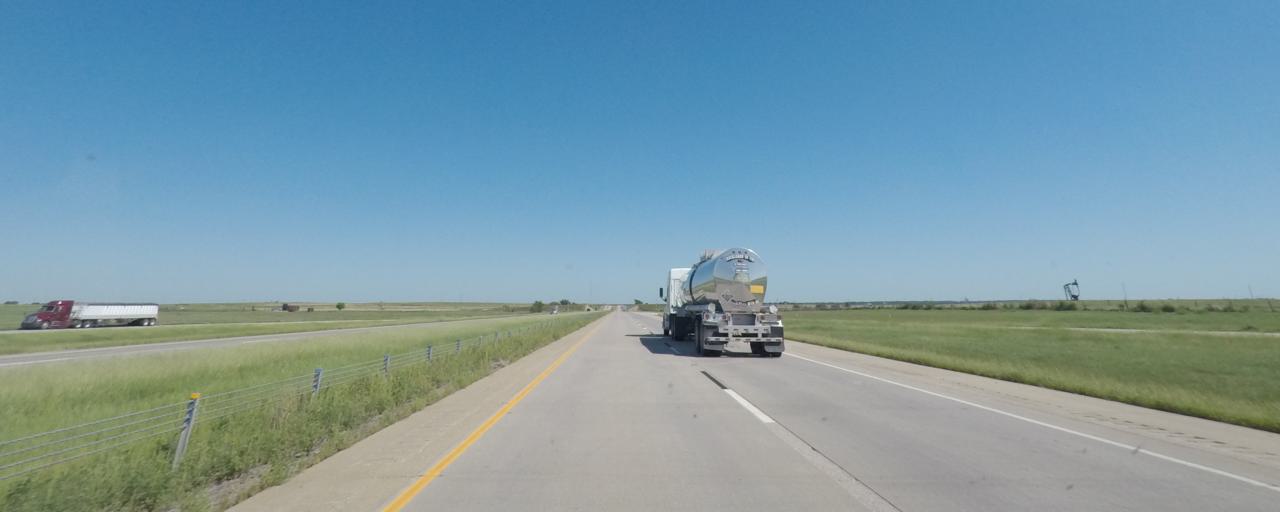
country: US
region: Oklahoma
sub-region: Kay County
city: Tonkawa
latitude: 36.6158
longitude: -97.3457
